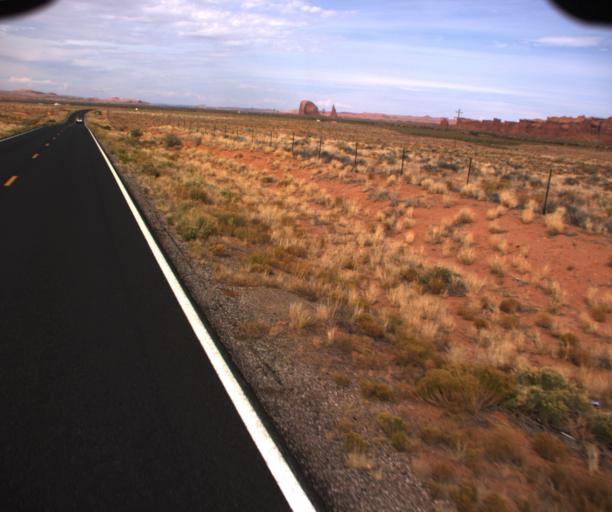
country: US
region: Arizona
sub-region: Apache County
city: Many Farms
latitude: 36.6083
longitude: -109.5750
